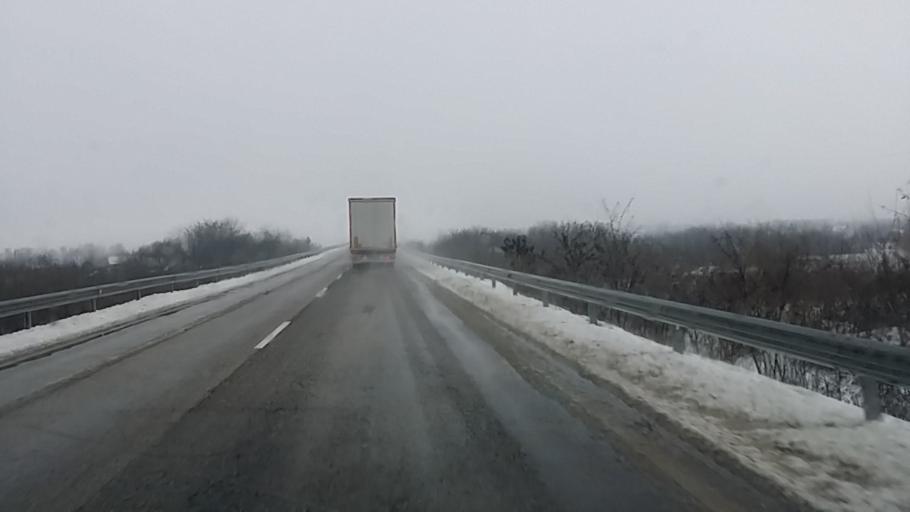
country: HU
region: Komarom-Esztergom
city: Komarom
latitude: 47.7394
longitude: 18.0940
